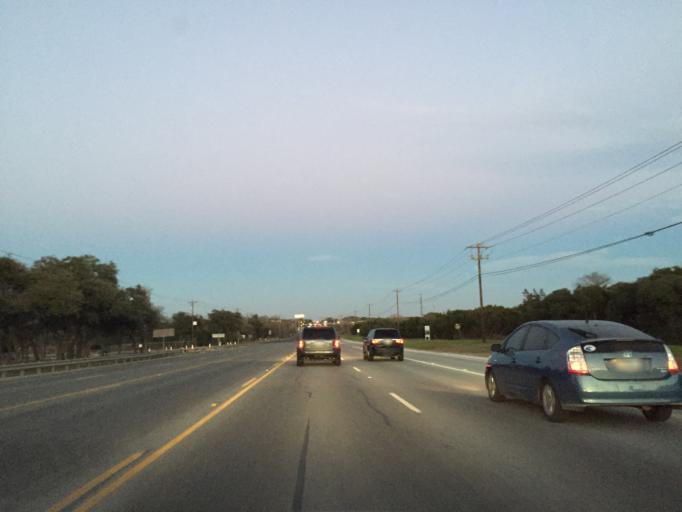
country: US
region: Texas
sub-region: Williamson County
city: Cedar Park
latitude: 30.5124
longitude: -97.8576
